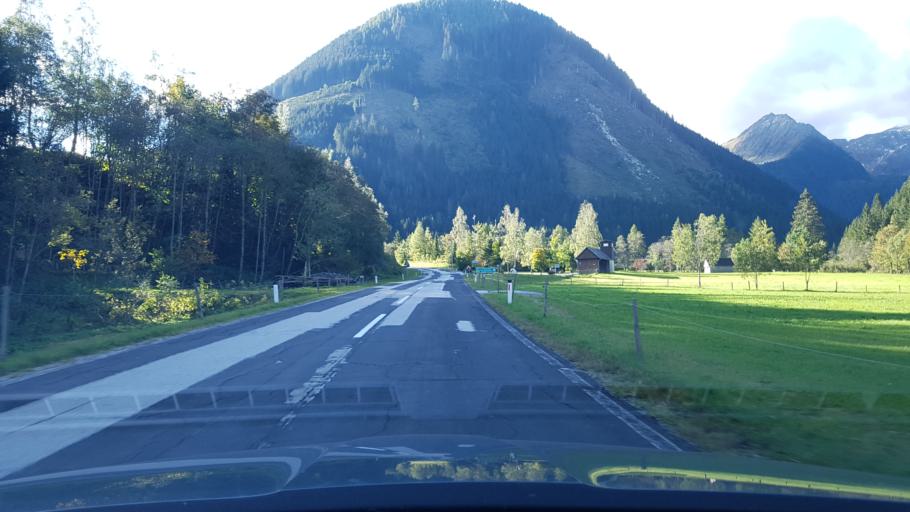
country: AT
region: Styria
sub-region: Politischer Bezirk Liezen
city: Sankt Nikolai im Solktal
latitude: 47.3226
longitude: 14.0469
